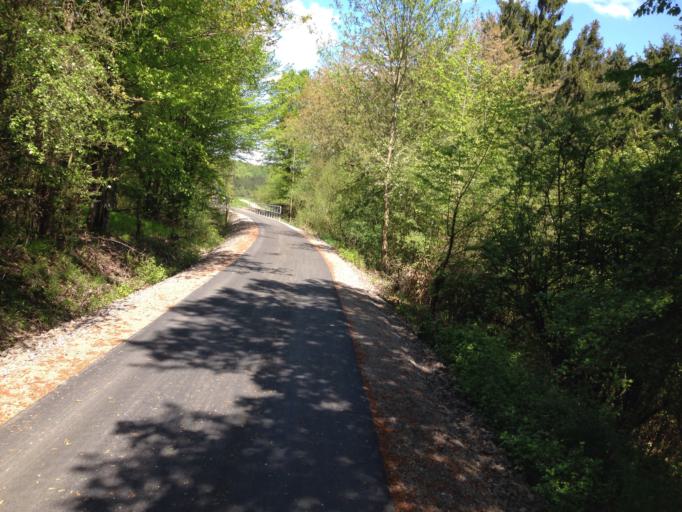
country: DE
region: Hesse
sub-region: Regierungsbezirk Giessen
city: Laubach
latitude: 50.5188
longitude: 8.9365
